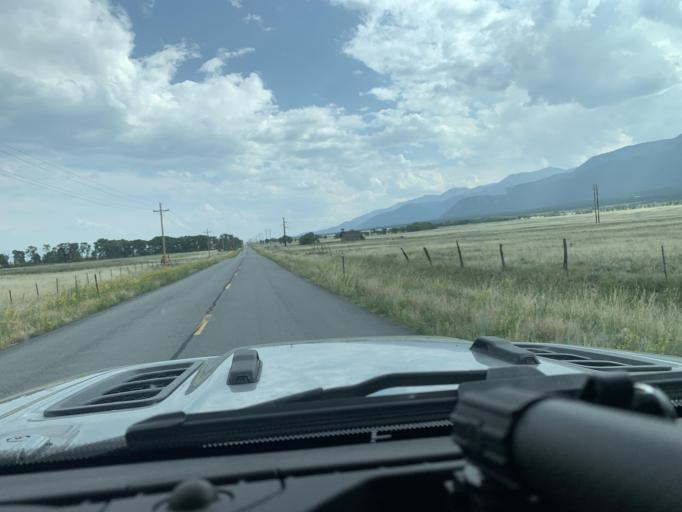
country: US
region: Colorado
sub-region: Chaffee County
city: Buena Vista
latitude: 38.7986
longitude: -106.1465
